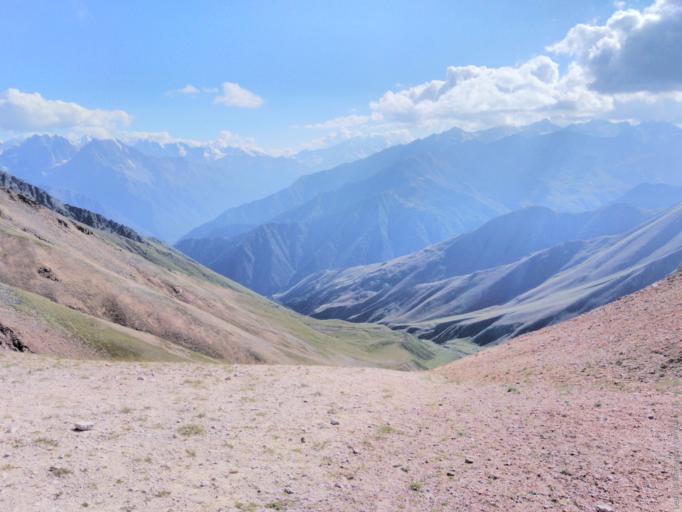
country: RU
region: Kabardino-Balkariya
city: Tyrnyauz
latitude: 43.3812
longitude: 42.7836
